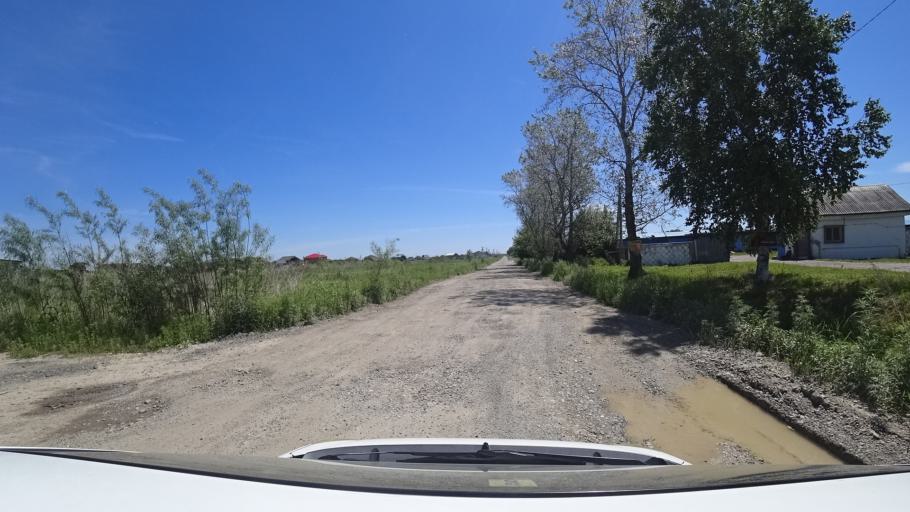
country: RU
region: Khabarovsk Krai
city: Topolevo
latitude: 48.5118
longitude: 135.1903
